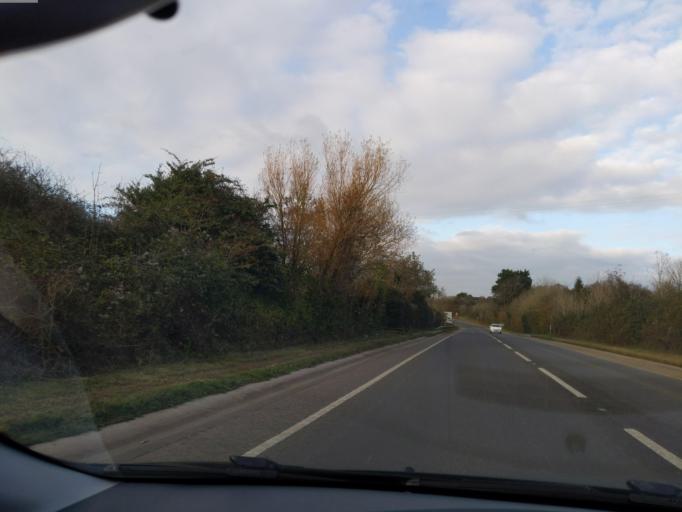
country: GB
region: England
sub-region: Cornwall
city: Wadebridge
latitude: 50.5189
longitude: -4.8198
